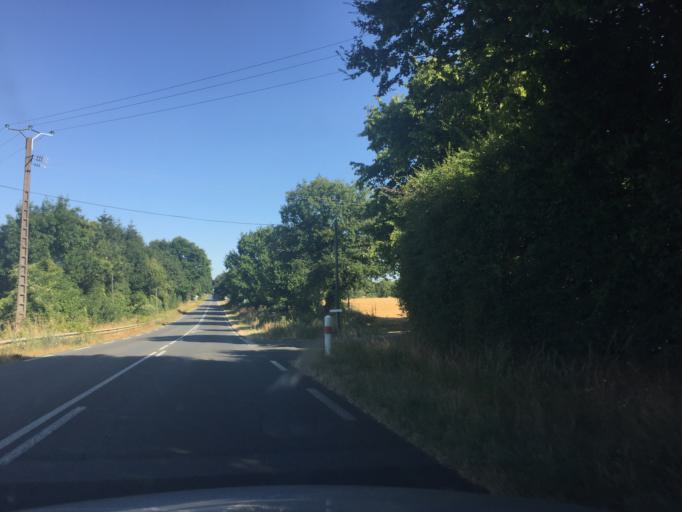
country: FR
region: Poitou-Charentes
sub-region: Departement des Deux-Sevres
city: Chef-Boutonne
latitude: 46.1871
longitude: -0.0440
